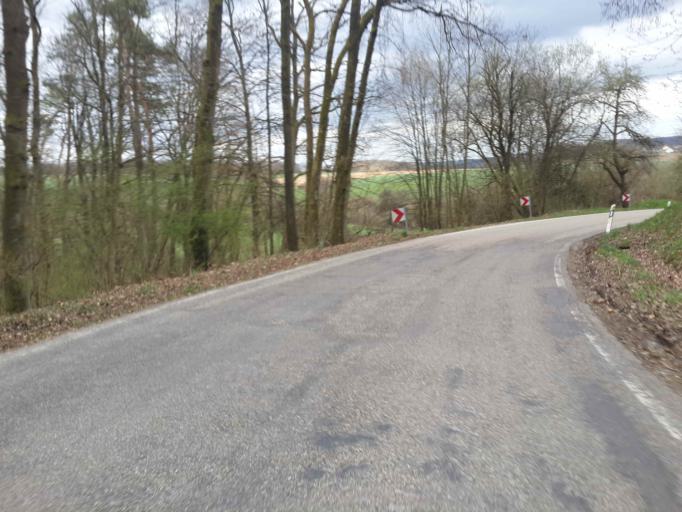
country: DE
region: Baden-Wuerttemberg
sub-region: Regierungsbezirk Stuttgart
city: Roigheim
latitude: 49.3699
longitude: 9.3229
